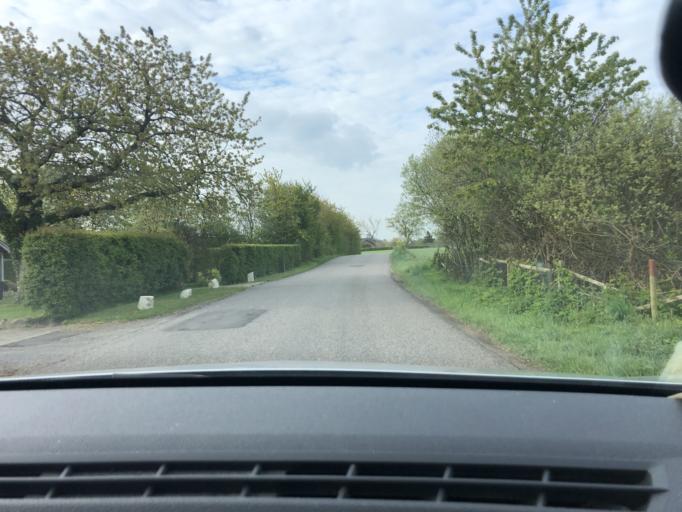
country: DK
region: Zealand
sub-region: Faxe Kommune
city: Ronnede
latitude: 55.2327
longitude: 12.0517
